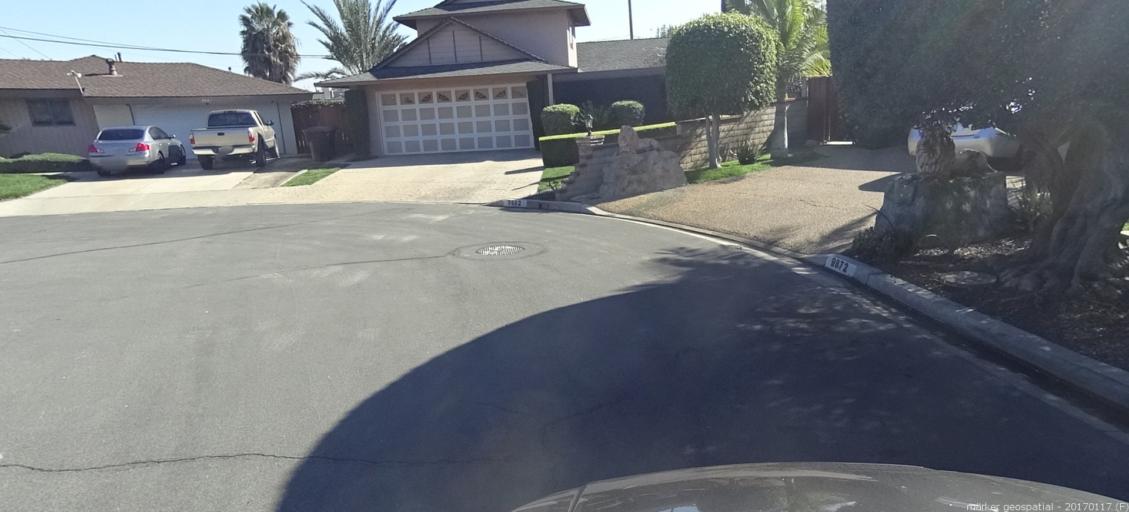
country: US
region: California
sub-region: Orange County
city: Stanton
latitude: 33.8262
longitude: -117.9608
